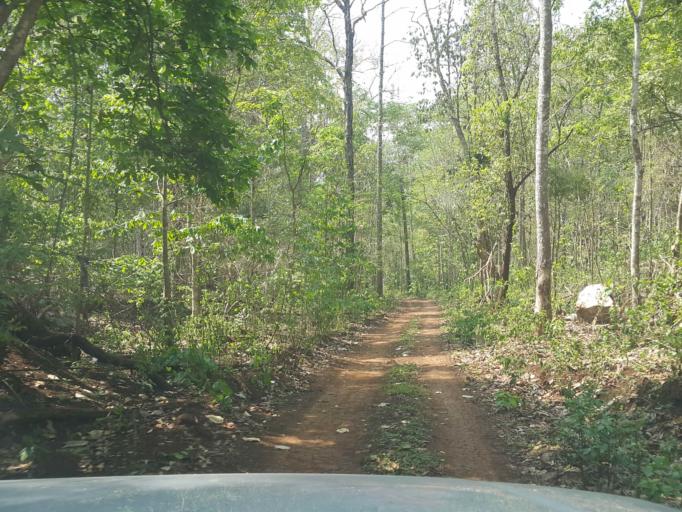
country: TH
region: Chiang Mai
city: Wiang Haeng
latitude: 19.3320
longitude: 98.7193
